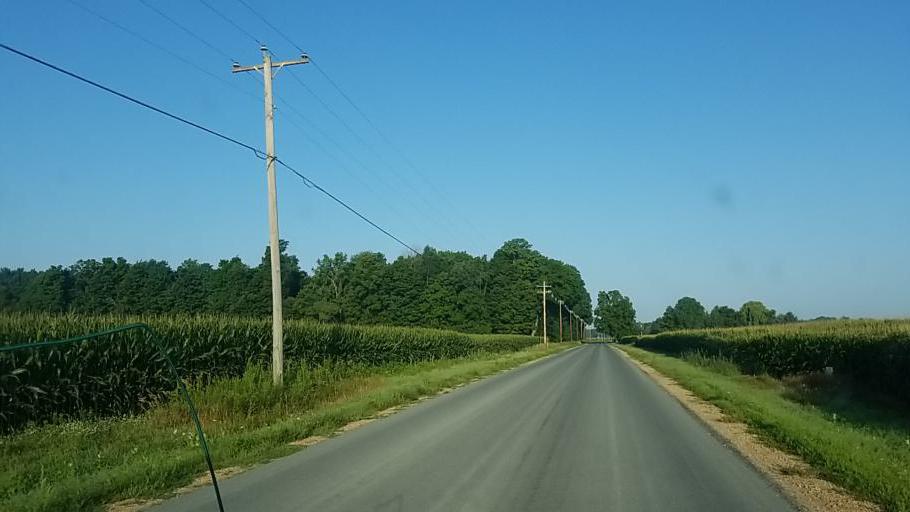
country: US
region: Michigan
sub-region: Montcalm County
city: Howard City
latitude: 43.3666
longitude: -85.4258
